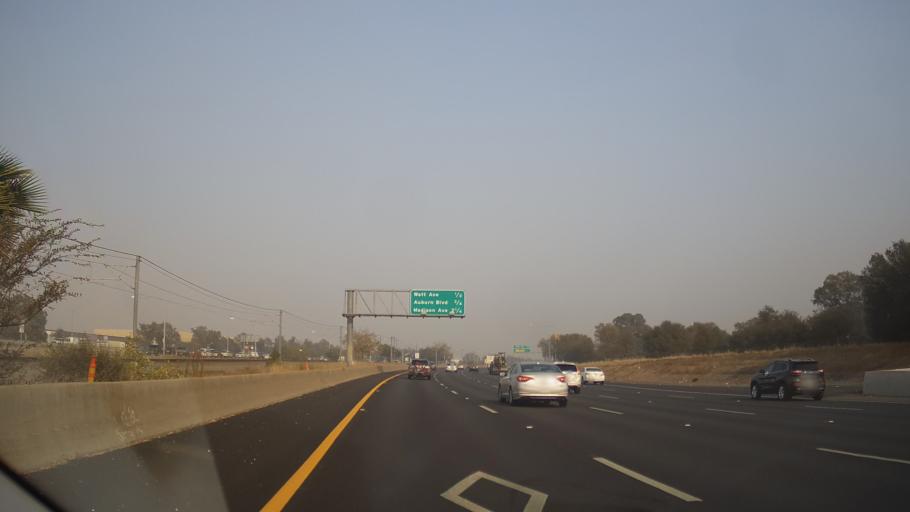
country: US
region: California
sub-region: Sacramento County
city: Arden-Arcade
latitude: 38.6412
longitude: -121.3970
